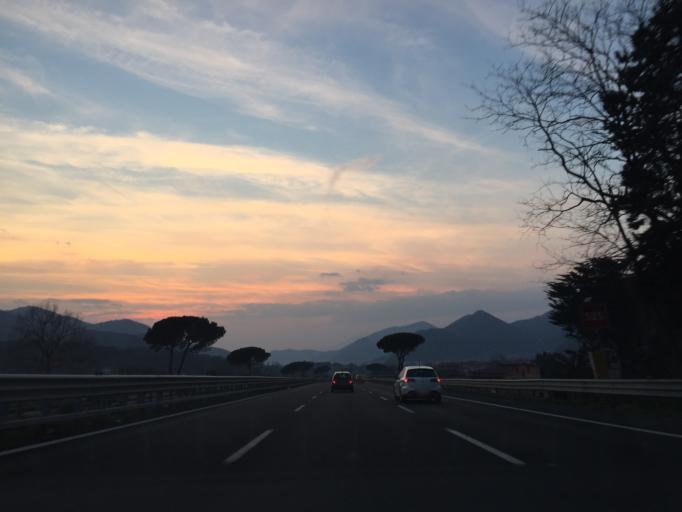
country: IT
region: Campania
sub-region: Provincia di Salerno
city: Faraldo-Nocelleto
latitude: 40.7729
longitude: 14.7725
